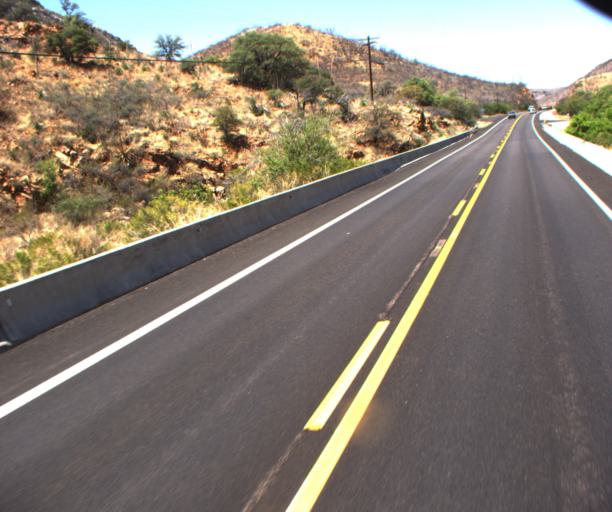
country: US
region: Arizona
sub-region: Cochise County
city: Bisbee
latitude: 31.5018
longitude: -110.0050
